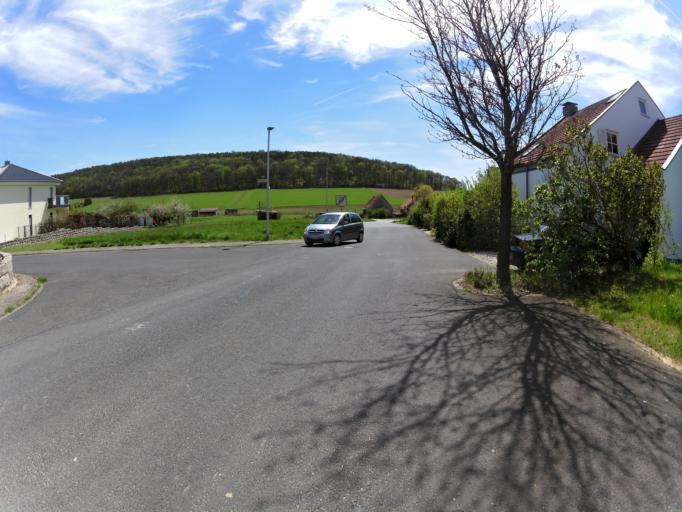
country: DE
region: Bavaria
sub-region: Regierungsbezirk Unterfranken
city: Greussenheim
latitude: 49.8127
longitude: 9.7550
